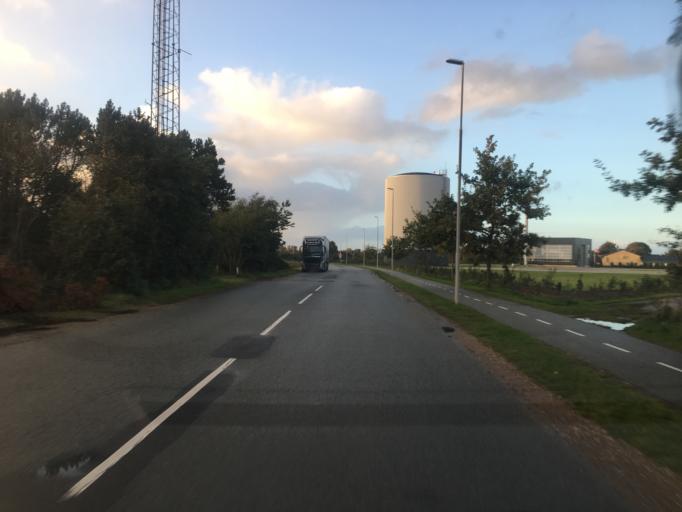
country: DK
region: South Denmark
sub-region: Tonder Kommune
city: Tonder
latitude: 54.9281
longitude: 8.8520
